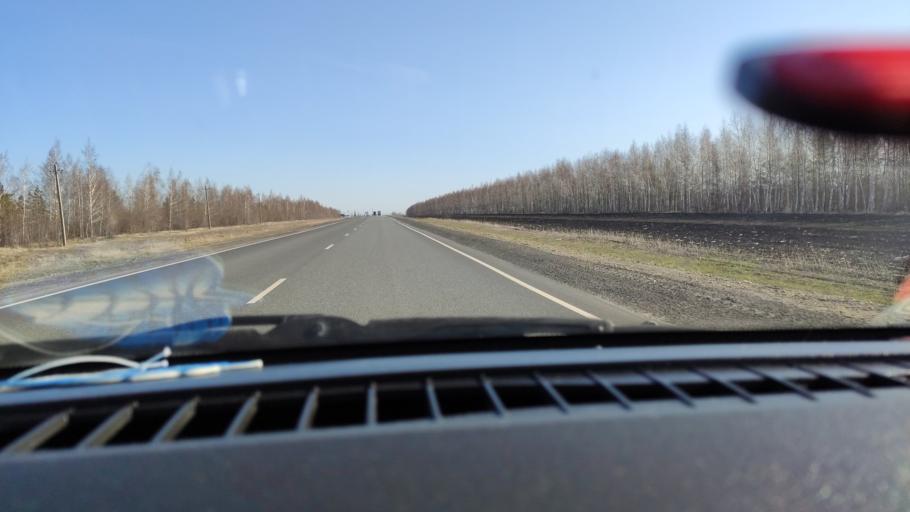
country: RU
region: Samara
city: Syzran'
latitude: 52.9889
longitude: 48.3199
